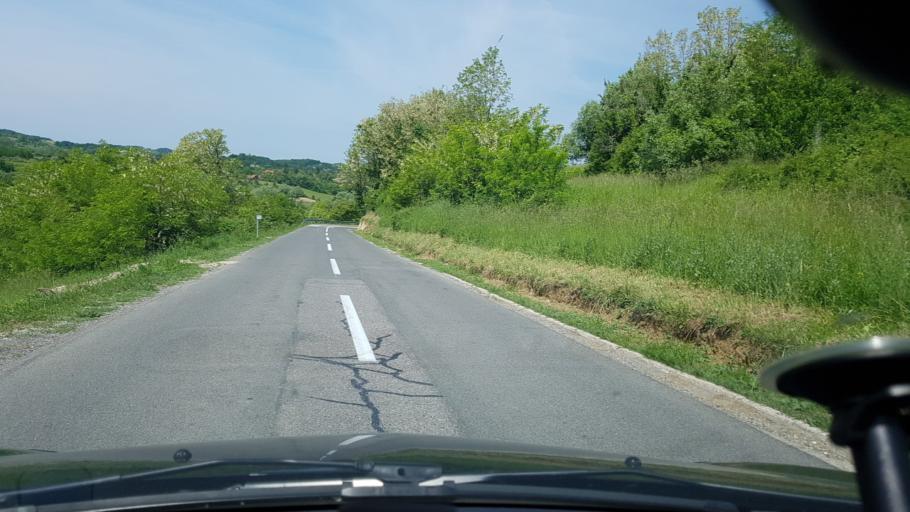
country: HR
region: Krapinsko-Zagorska
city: Marija Bistrica
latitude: 46.0059
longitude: 16.0829
